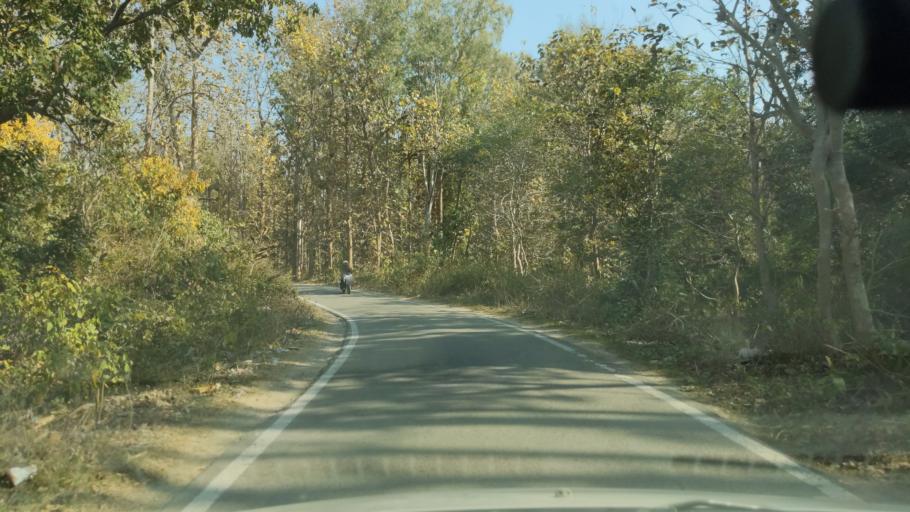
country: IN
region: Uttarakhand
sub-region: Naini Tal
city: Ramnagar
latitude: 29.4024
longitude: 79.1366
